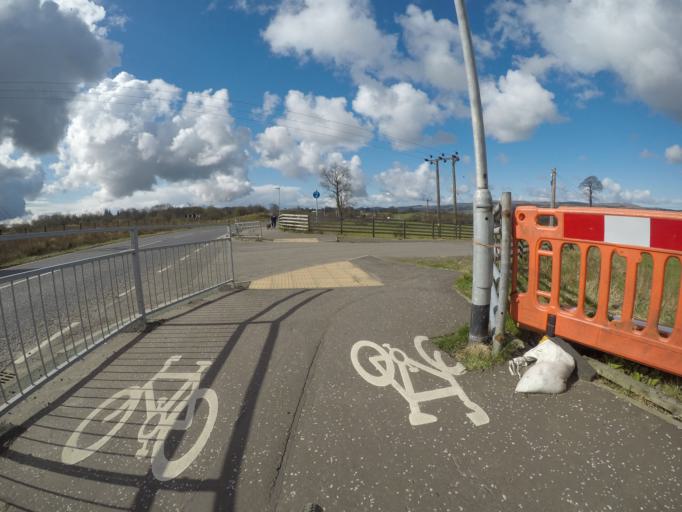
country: GB
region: Scotland
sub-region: North Ayrshire
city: Beith
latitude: 55.7395
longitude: -4.6558
